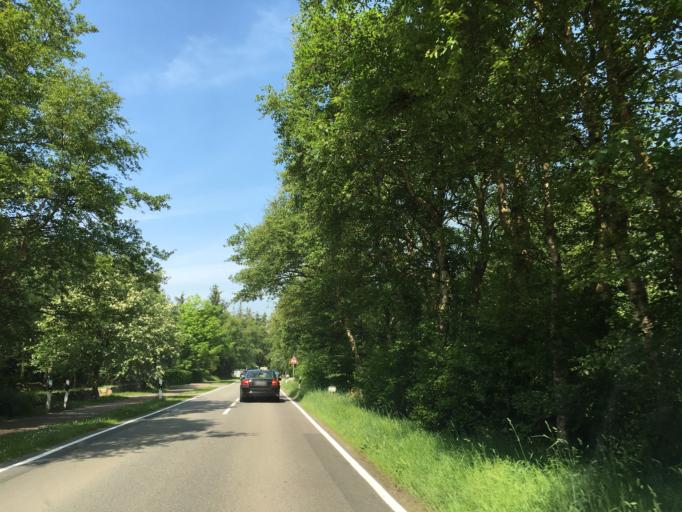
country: DE
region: Schleswig-Holstein
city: Wittdun
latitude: 54.6281
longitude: 8.3785
